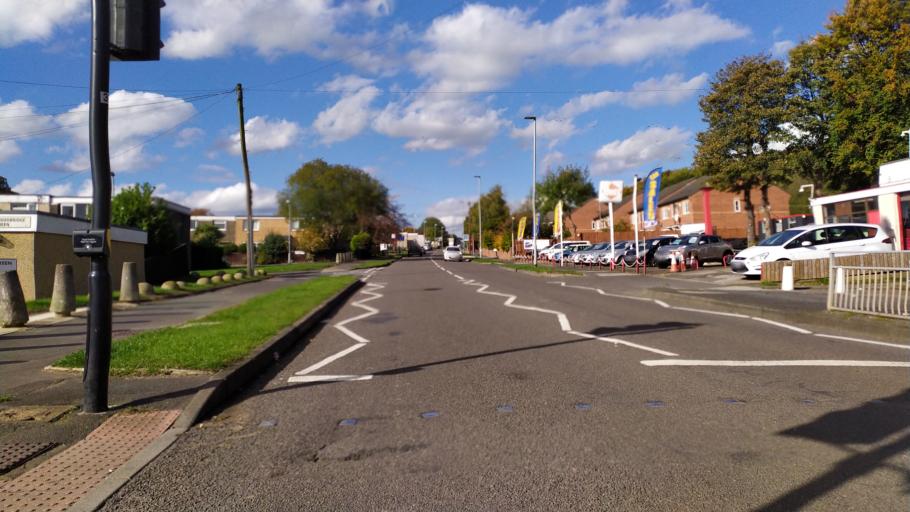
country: GB
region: England
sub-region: City and Borough of Leeds
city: Horsforth
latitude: 53.8217
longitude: -1.5974
